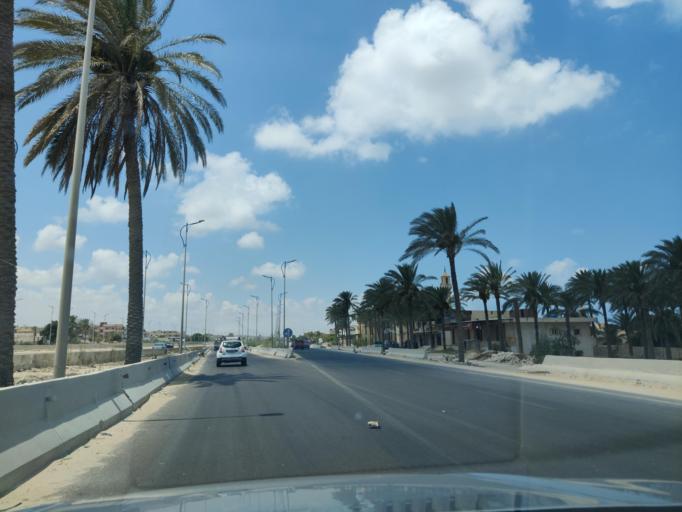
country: EG
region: Alexandria
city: Alexandria
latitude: 31.0055
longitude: 29.6177
